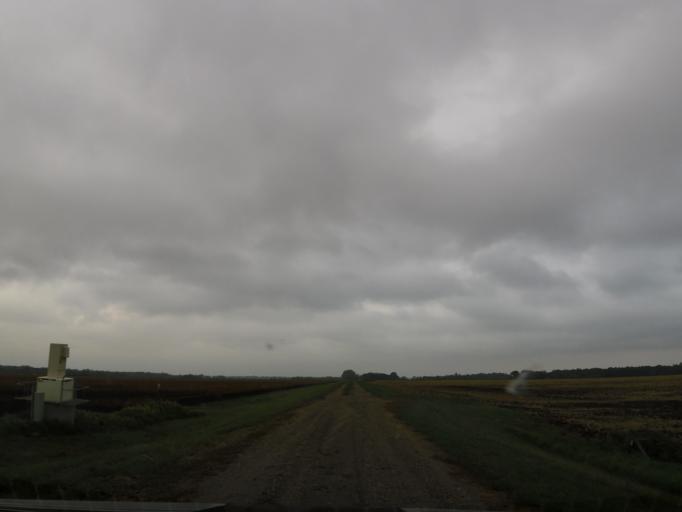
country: US
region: North Dakota
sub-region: Walsh County
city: Grafton
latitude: 48.5139
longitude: -97.1685
